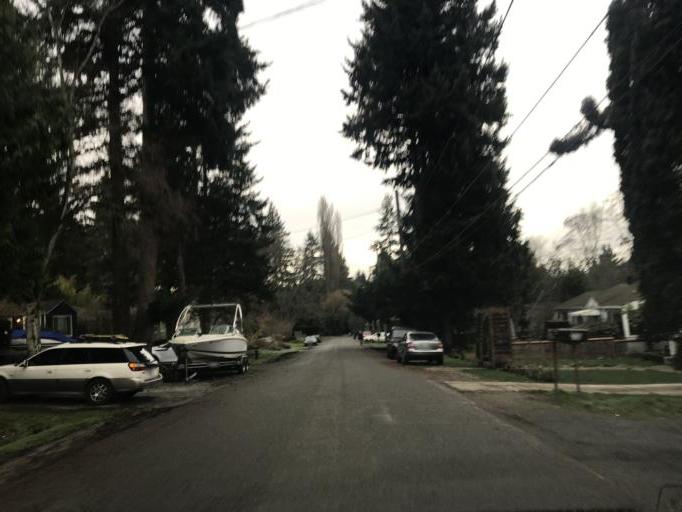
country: US
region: Washington
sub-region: King County
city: Lake Forest Park
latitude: 47.7151
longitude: -122.2873
